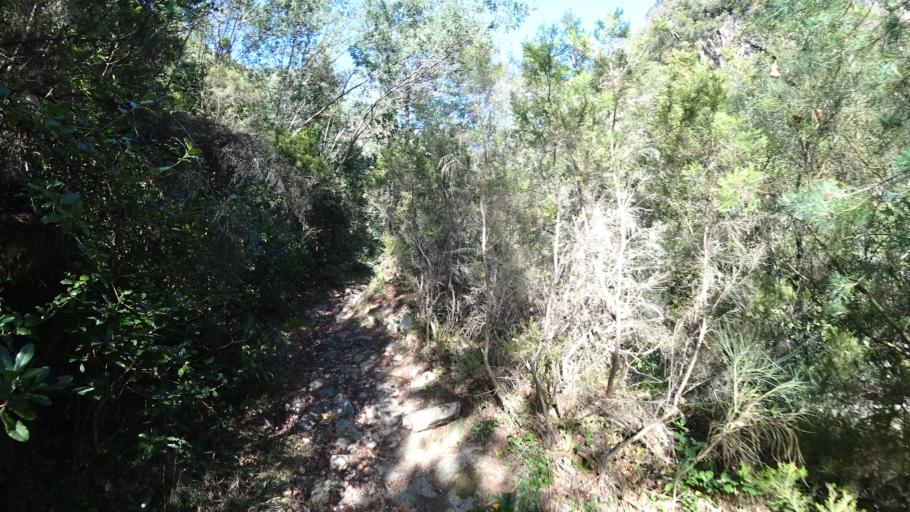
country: PT
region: Braga
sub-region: Vieira do Minho
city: Real
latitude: 41.7594
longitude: -8.1495
